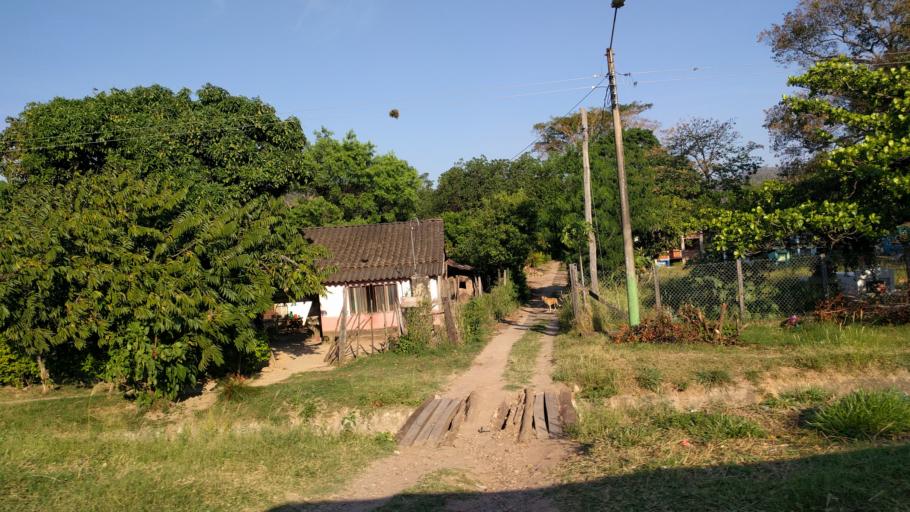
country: BO
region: Santa Cruz
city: Jorochito
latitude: -18.1132
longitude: -63.4596
